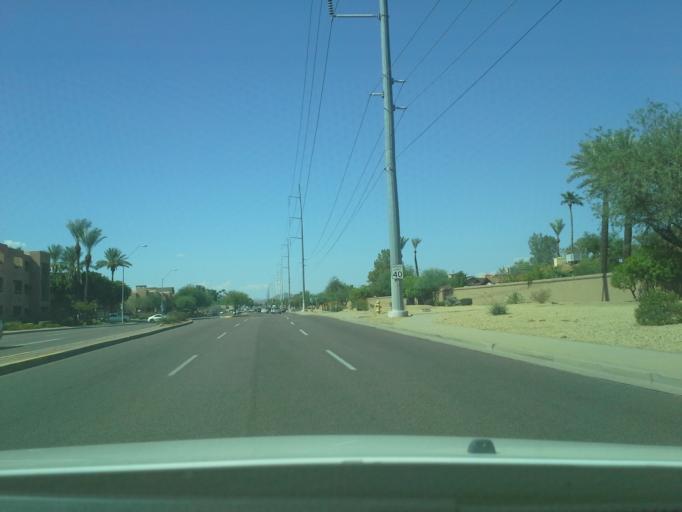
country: US
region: Arizona
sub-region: Maricopa County
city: Glendale
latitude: 33.6344
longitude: -112.0654
